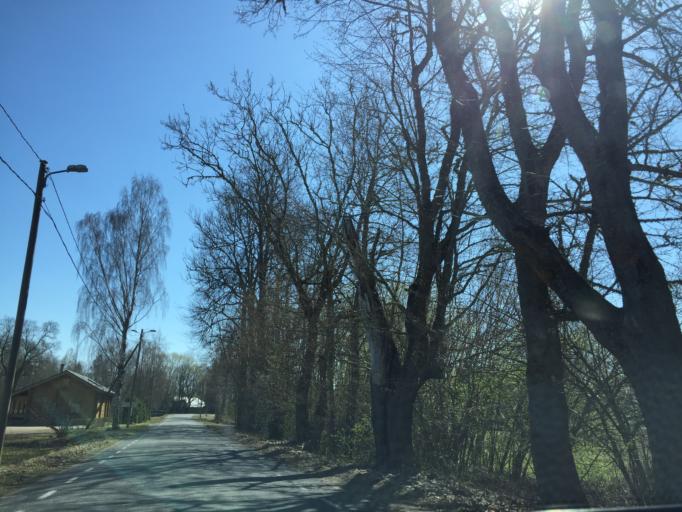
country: EE
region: Jogevamaa
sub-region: Poltsamaa linn
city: Poltsamaa
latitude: 58.3709
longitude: 25.9560
